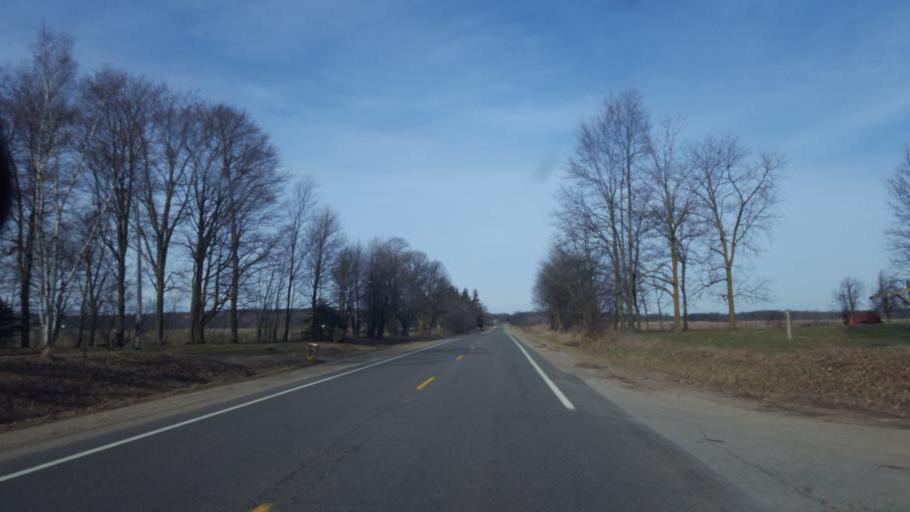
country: US
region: Michigan
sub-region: Montcalm County
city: Lakeview
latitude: 43.4315
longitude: -85.3129
